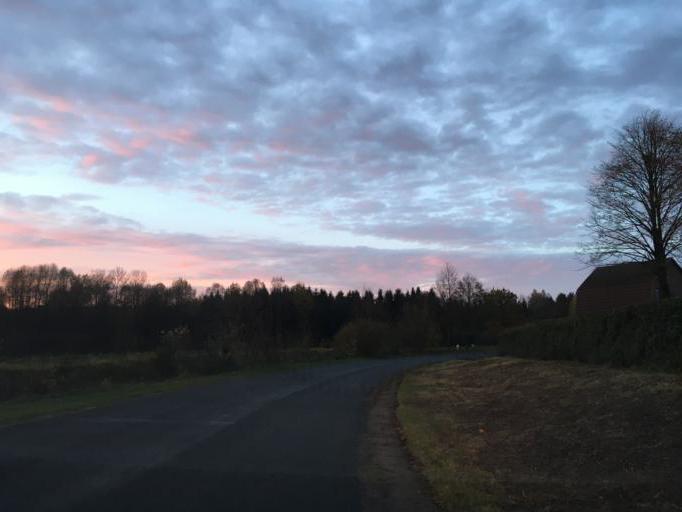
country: DE
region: Lower Saxony
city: Soderstorf
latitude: 53.1190
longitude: 10.1155
